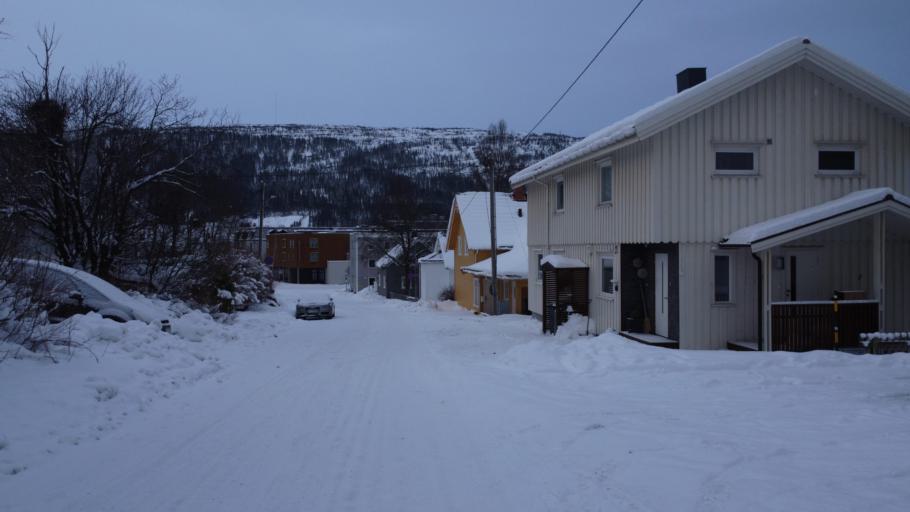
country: NO
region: Nordland
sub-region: Rana
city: Mo i Rana
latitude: 66.3141
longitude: 14.1350
